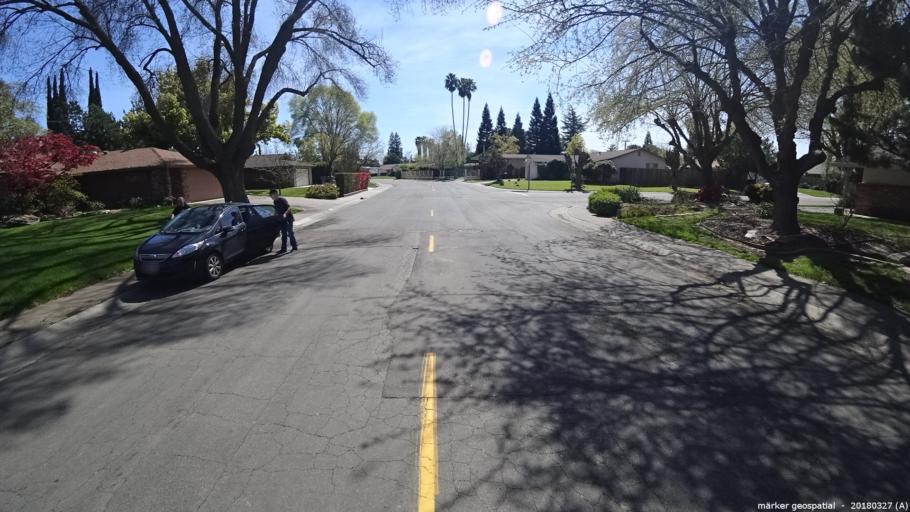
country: US
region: California
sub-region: Sacramento County
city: Rosemont
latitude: 38.5523
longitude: -121.3566
